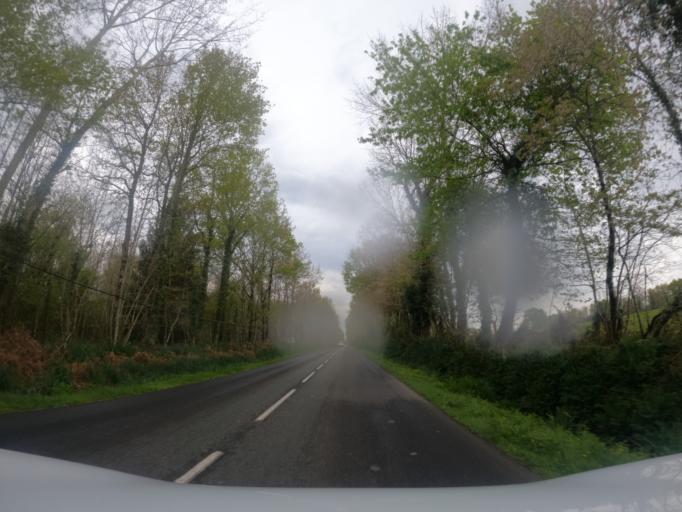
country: FR
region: Pays de la Loire
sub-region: Departement de la Vendee
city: Le Champ-Saint-Pere
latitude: 46.5268
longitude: -1.3623
